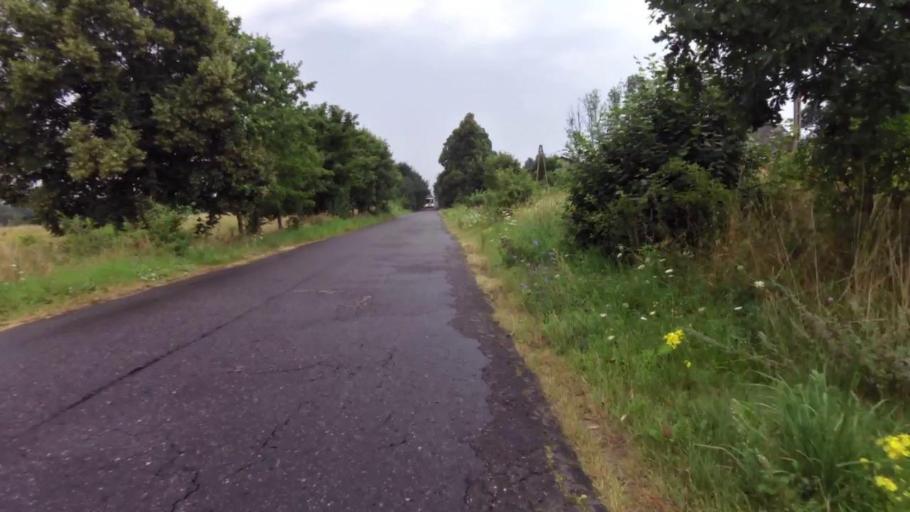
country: PL
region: West Pomeranian Voivodeship
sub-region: Powiat stargardzki
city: Insko
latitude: 53.4806
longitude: 15.6092
